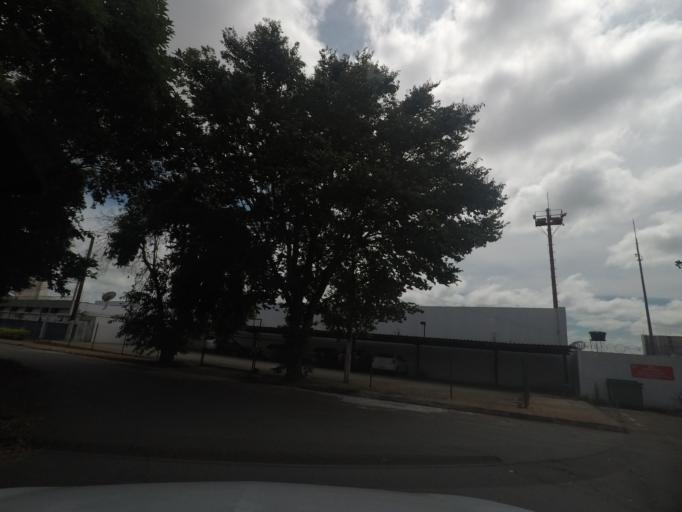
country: BR
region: Goias
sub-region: Goiania
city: Goiania
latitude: -16.6333
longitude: -49.2262
